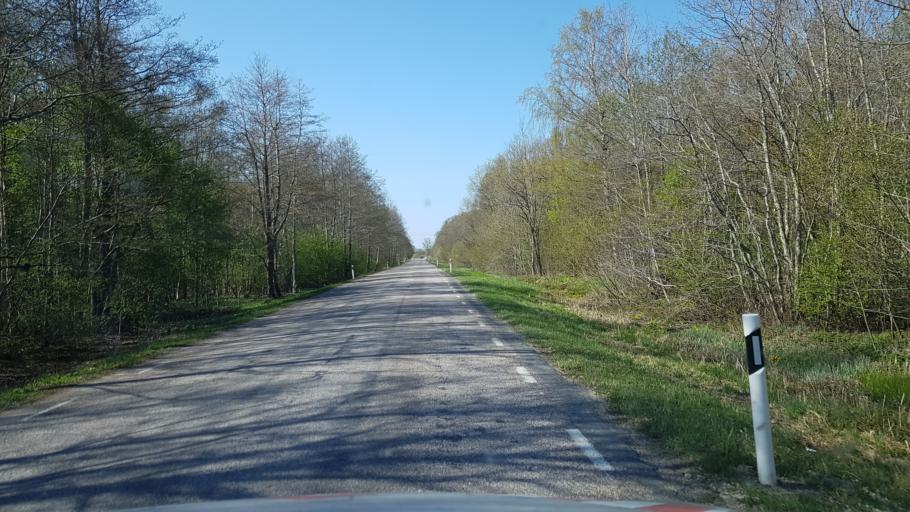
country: EE
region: Harju
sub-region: Keila linn
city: Keila
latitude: 59.4423
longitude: 24.3885
